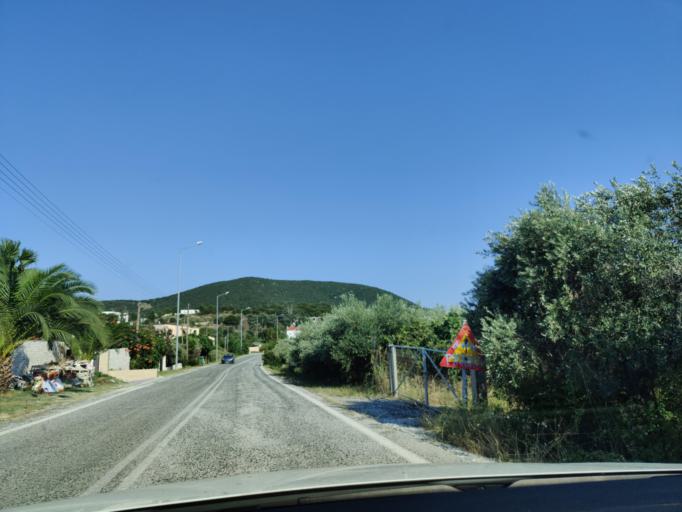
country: GR
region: East Macedonia and Thrace
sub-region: Nomos Kavalas
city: Nea Iraklitsa
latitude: 40.8560
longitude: 24.3112
